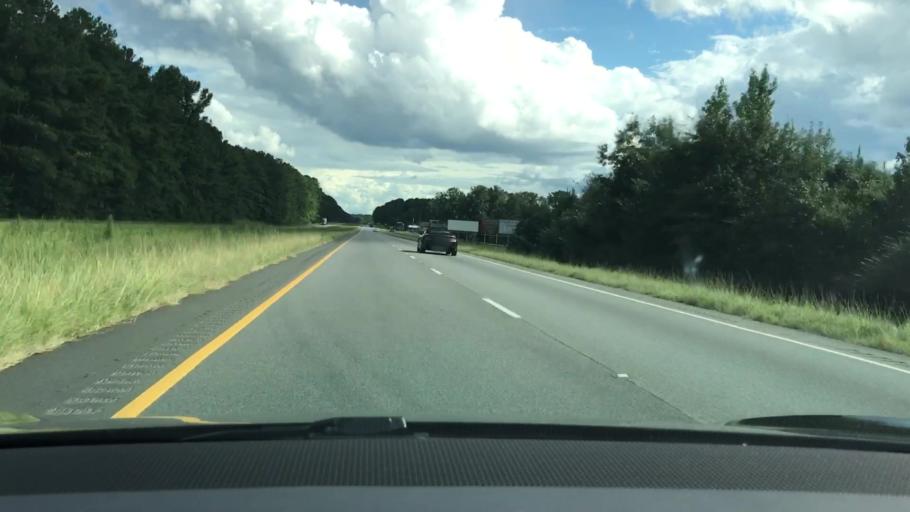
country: US
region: Alabama
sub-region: Pike County
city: Troy
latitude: 31.9248
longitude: -86.0176
